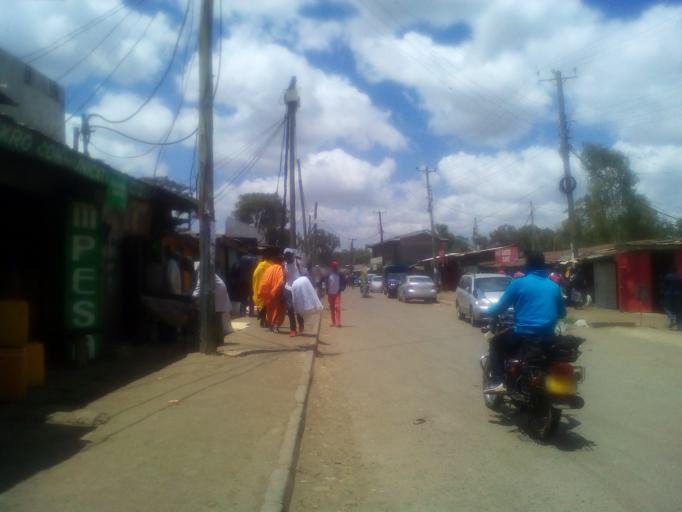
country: KE
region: Nairobi Area
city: Nairobi
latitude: -1.3083
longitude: 36.7838
